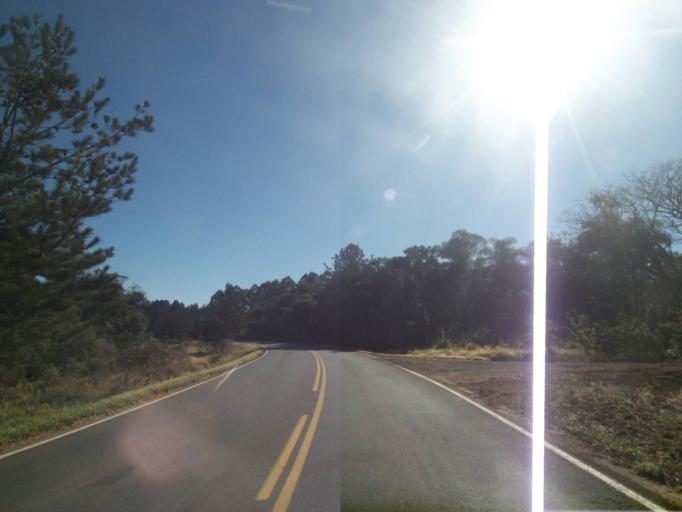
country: BR
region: Parana
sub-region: Tibagi
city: Tibagi
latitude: -24.4608
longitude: -50.5389
